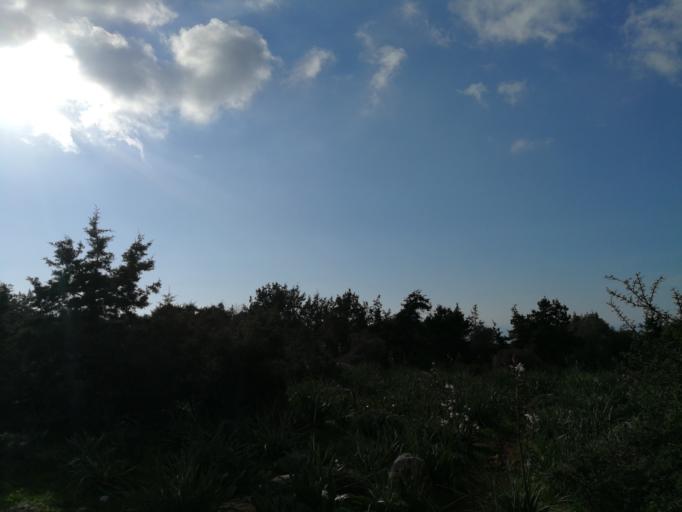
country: CY
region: Pafos
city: Pegeia
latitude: 34.9246
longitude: 32.3570
